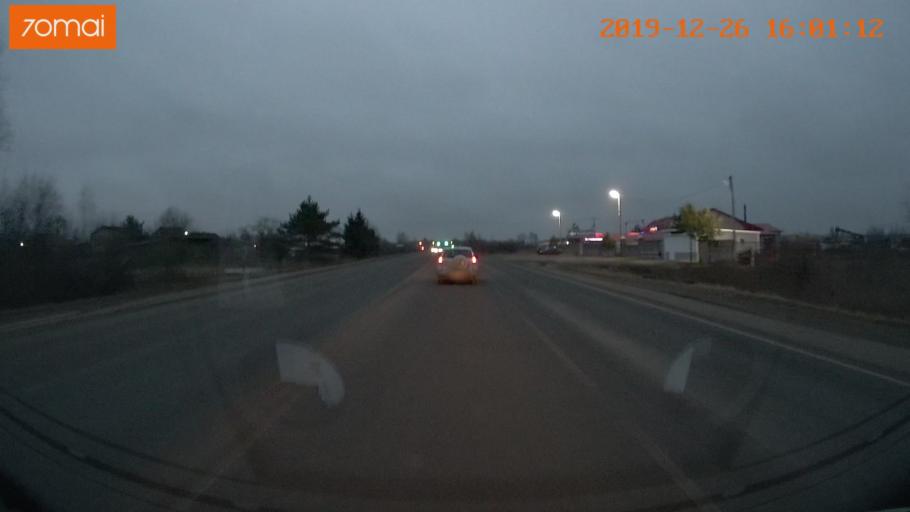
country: RU
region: Jaroslavl
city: Rybinsk
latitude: 58.0168
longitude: 38.8151
